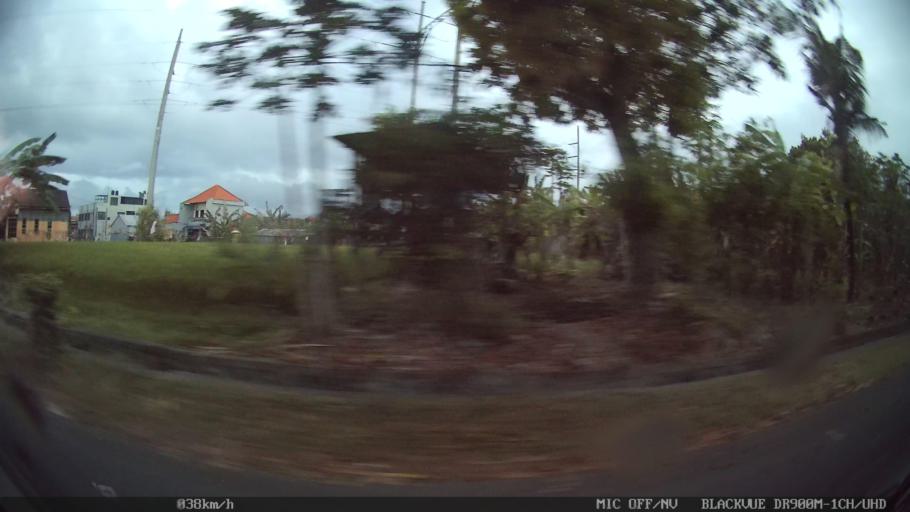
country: ID
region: Bali
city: Banjar Pasekan
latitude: -8.6417
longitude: 115.2800
